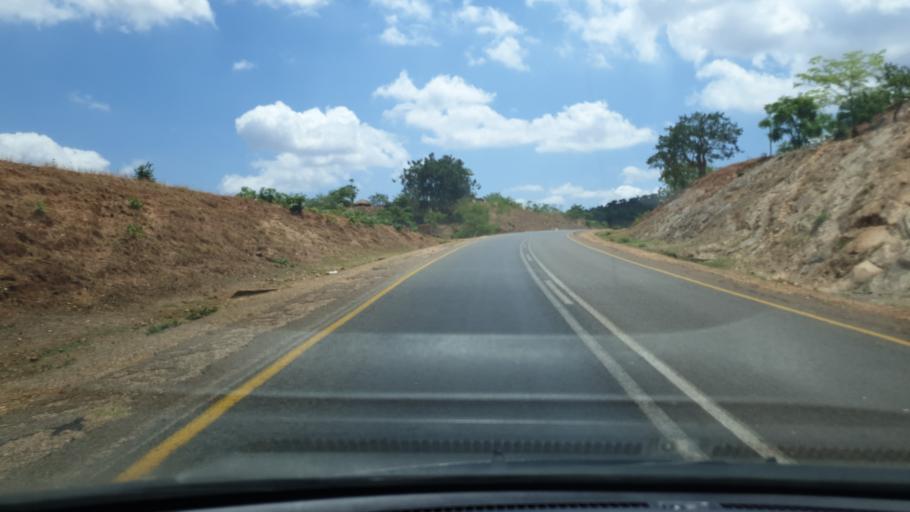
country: MW
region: Central Region
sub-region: Dowa District
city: Dowa
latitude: -13.7519
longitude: 34.0183
